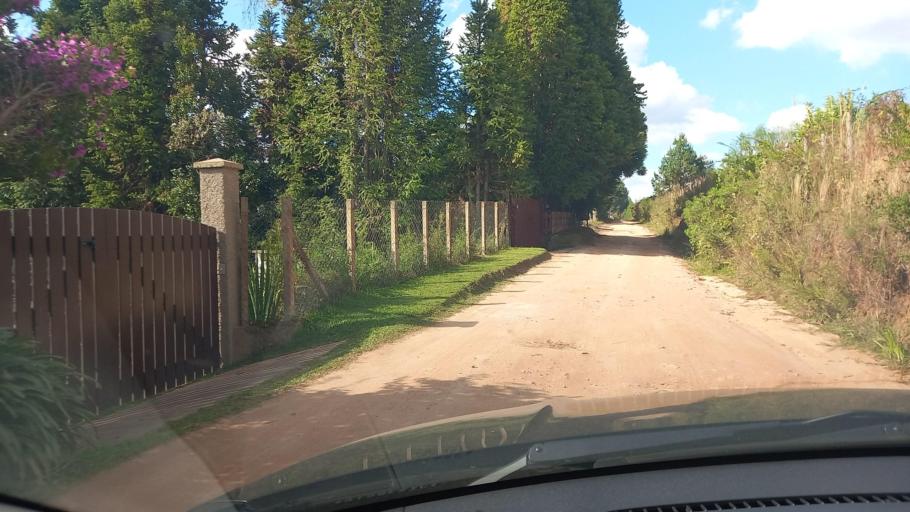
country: BR
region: Minas Gerais
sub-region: Camanducaia
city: Camanducaia
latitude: -22.8610
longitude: -46.0416
